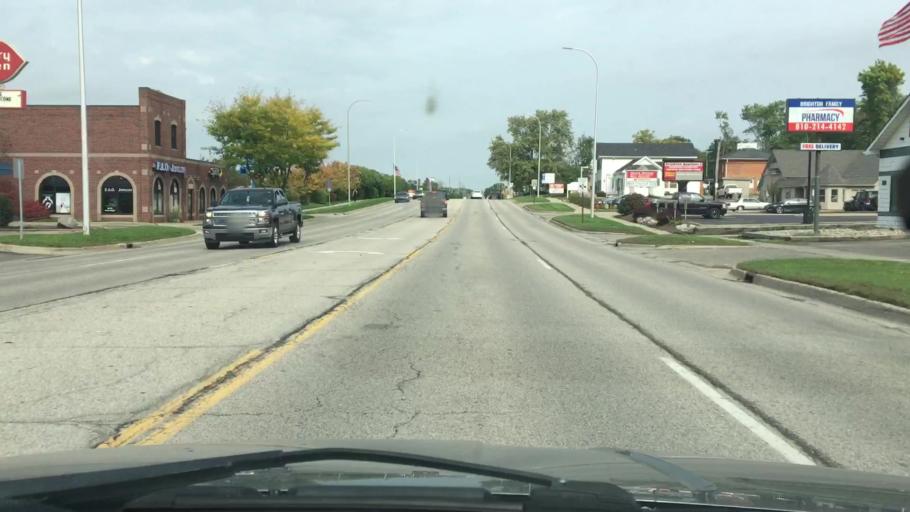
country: US
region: Michigan
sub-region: Livingston County
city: Brighton
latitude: 42.5315
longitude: -83.7813
